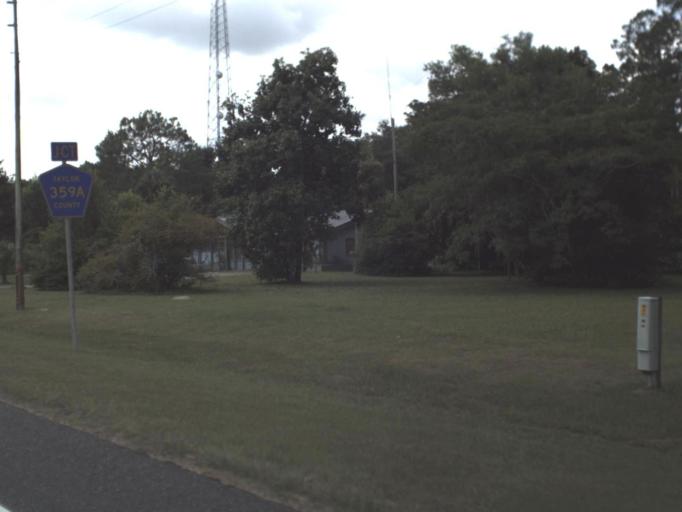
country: US
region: Florida
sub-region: Taylor County
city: Perry
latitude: 30.1475
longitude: -83.6126
